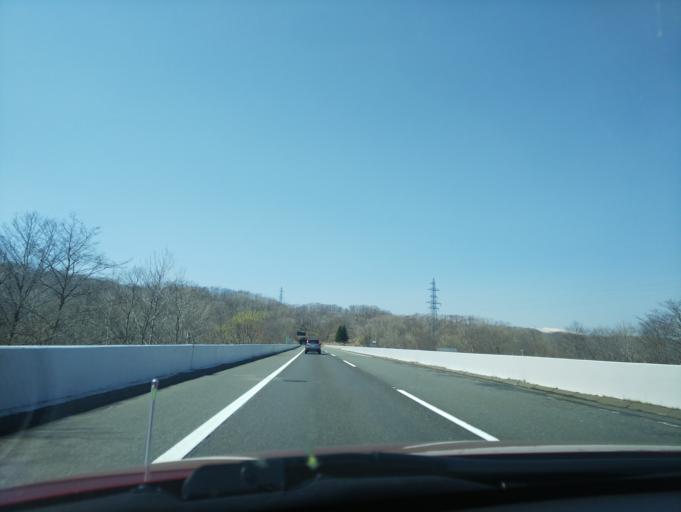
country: JP
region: Hokkaido
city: Shiraoi
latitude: 42.5754
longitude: 141.3690
